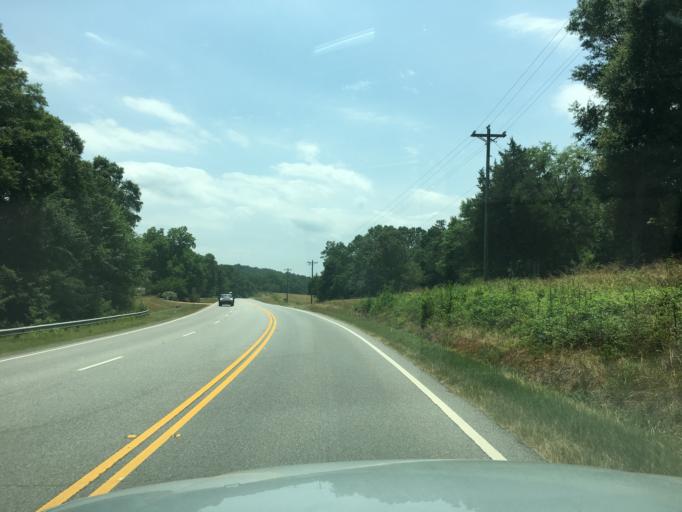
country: US
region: Georgia
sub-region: Hart County
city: Royston
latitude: 34.2598
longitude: -83.1694
